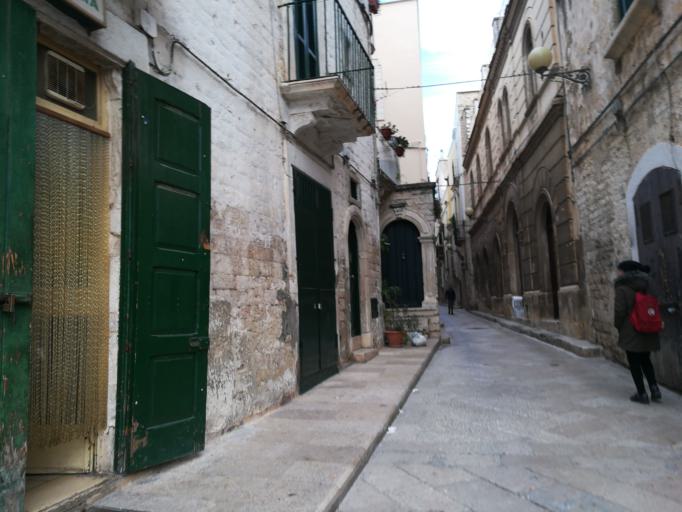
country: IT
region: Apulia
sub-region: Provincia di Bari
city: Bitonto
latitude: 41.1065
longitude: 16.6891
